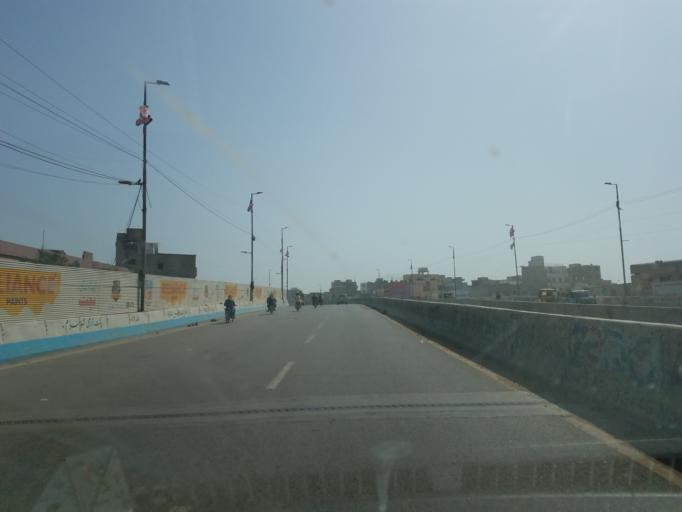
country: PK
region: Sindh
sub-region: Karachi District
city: Karachi
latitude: 24.9014
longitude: 67.0454
